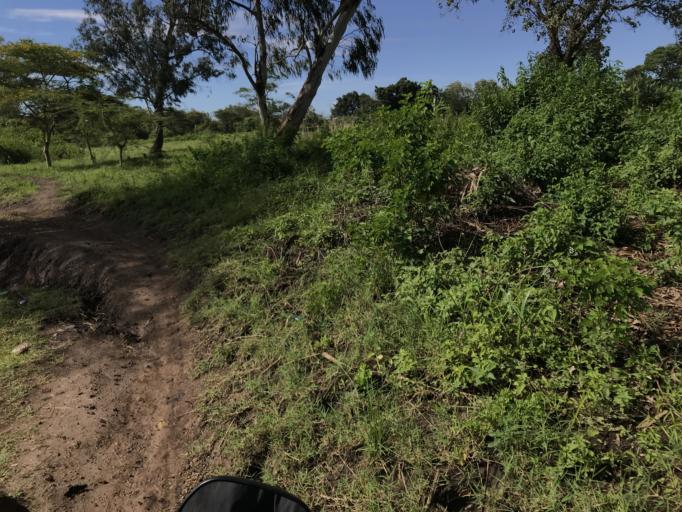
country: TZ
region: Arusha
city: Usa River
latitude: -3.3965
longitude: 36.7972
